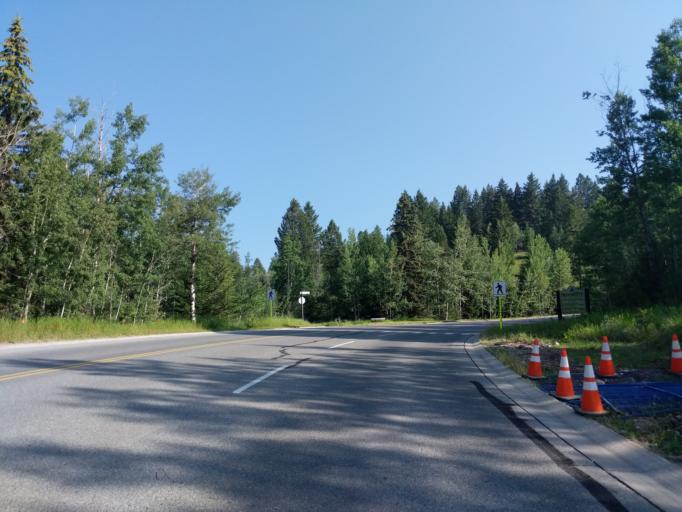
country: CA
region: Alberta
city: Canmore
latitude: 51.0986
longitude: -115.3413
